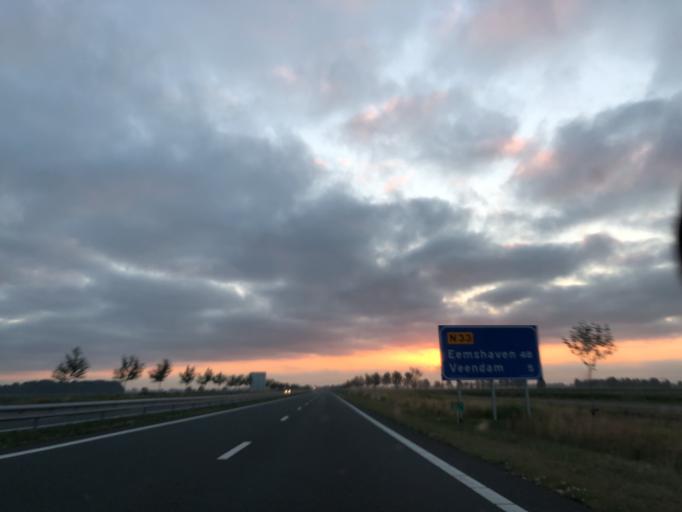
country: NL
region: Groningen
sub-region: Gemeente Veendam
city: Veendam
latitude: 53.0565
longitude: 6.8631
